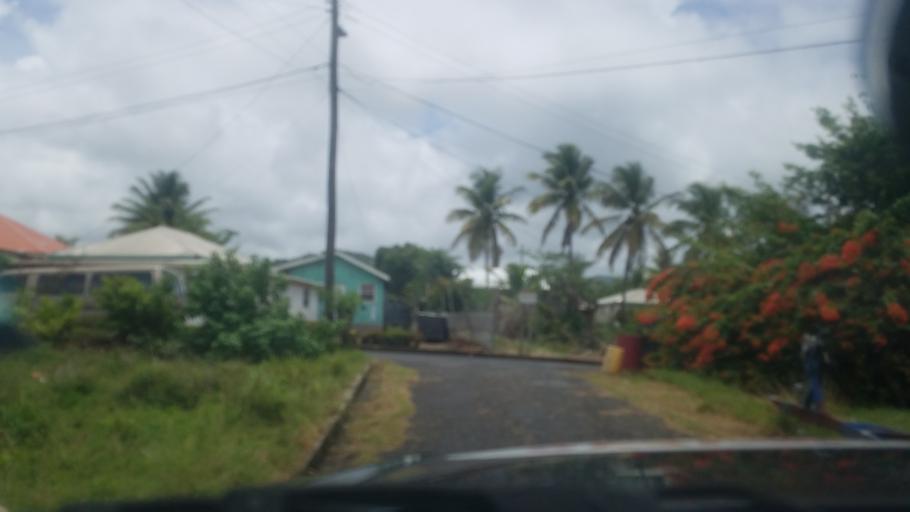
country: LC
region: Vieux-Fort
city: Vieux Fort
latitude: 13.7417
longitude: -60.9563
